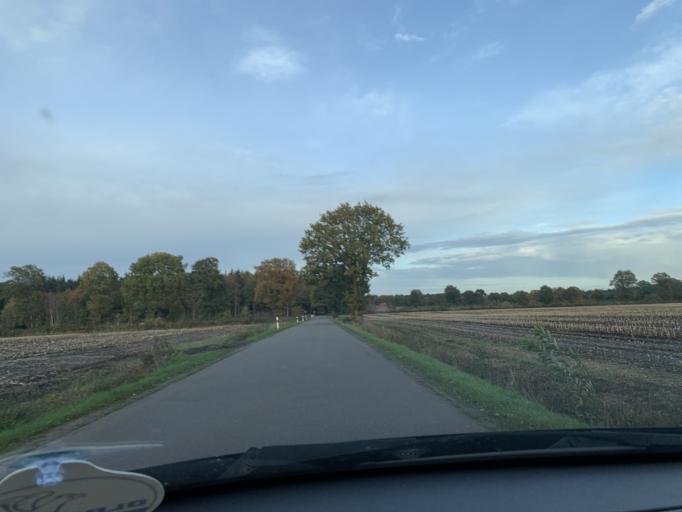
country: DE
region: Lower Saxony
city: Wiefelstede
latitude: 53.2419
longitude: 8.0585
